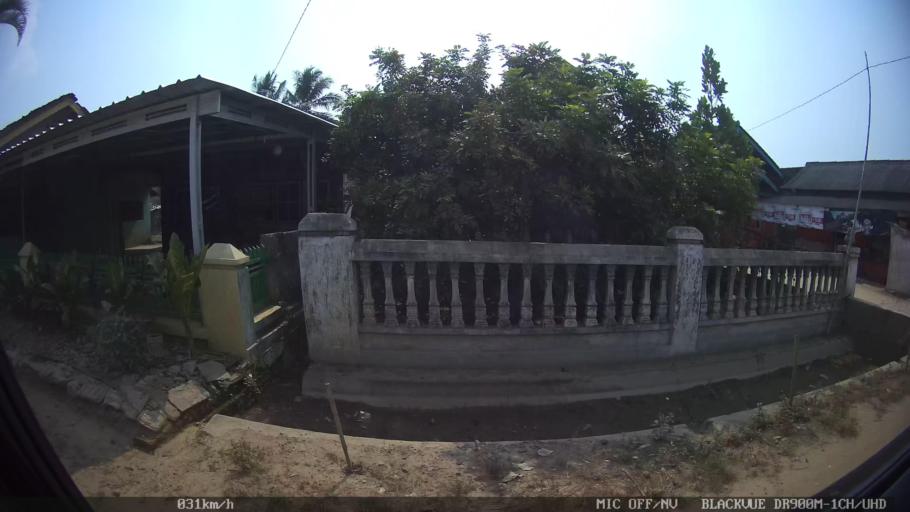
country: ID
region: Lampung
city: Pringsewu
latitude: -5.3989
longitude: 104.9929
